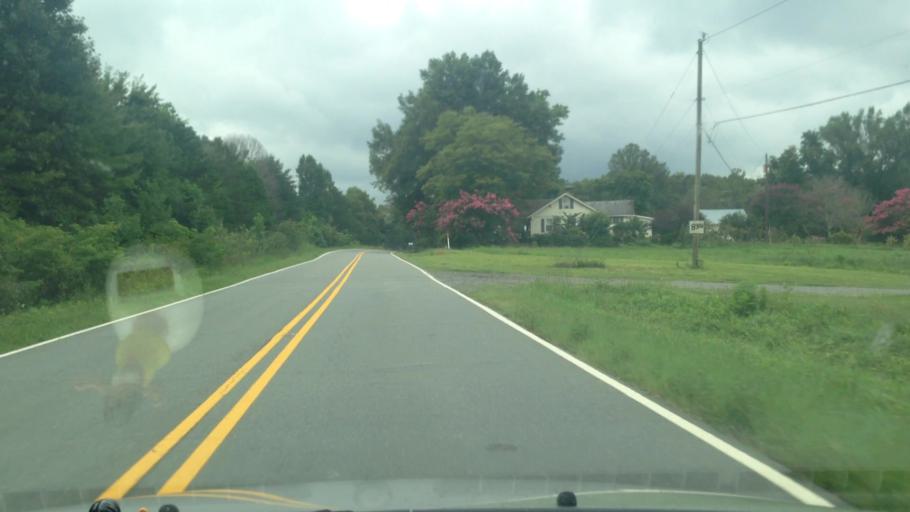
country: US
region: North Carolina
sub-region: Stokes County
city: Walnut Cove
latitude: 36.2432
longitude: -80.1536
